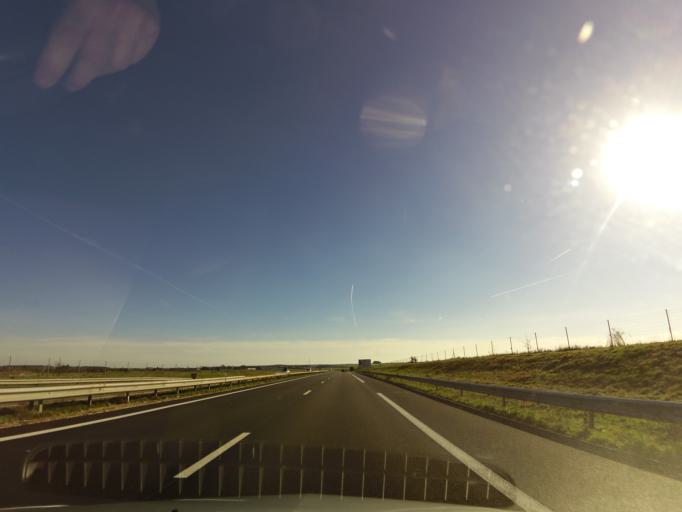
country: FR
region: Bourgogne
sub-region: Departement de l'Yonne
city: Joux-la-Ville
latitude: 47.6743
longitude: 3.8633
